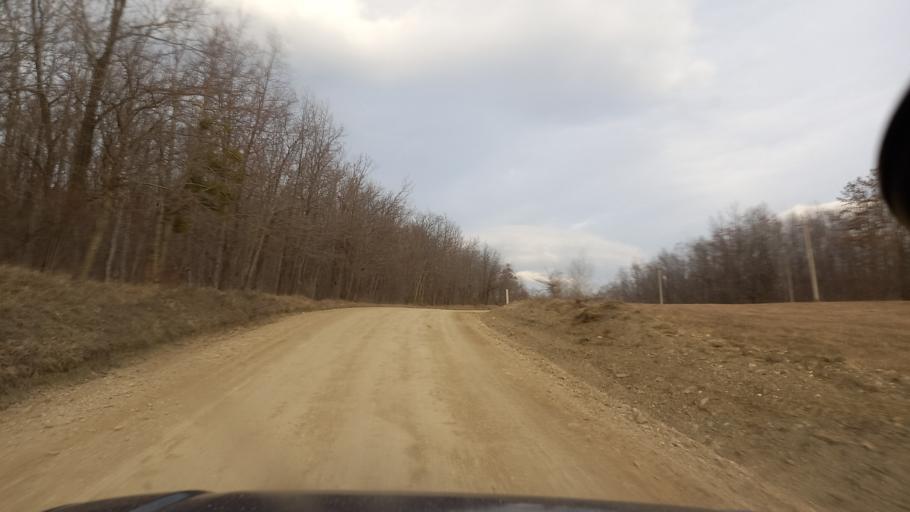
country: RU
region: Adygeya
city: Kamennomostskiy
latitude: 44.1755
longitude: 40.2511
